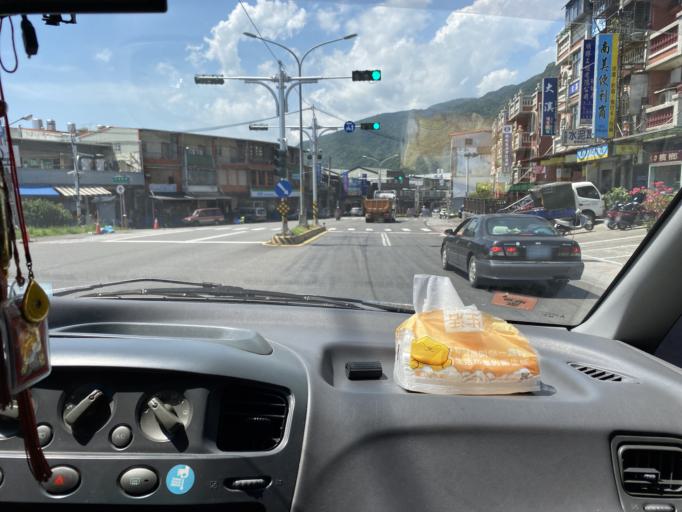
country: TW
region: Taiwan
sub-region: Yilan
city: Yilan
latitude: 24.9419
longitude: 121.9013
